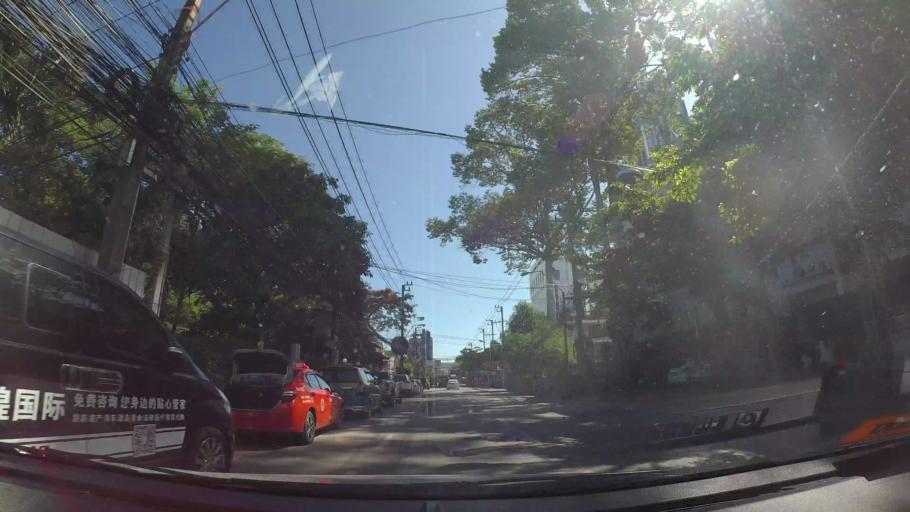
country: TH
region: Chon Buri
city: Phatthaya
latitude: 12.9384
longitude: 100.8871
